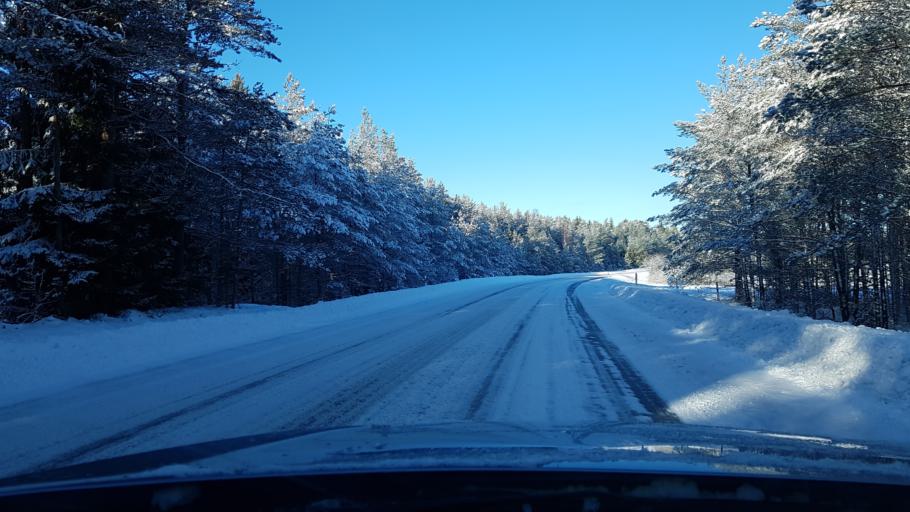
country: EE
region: Hiiumaa
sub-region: Kaerdla linn
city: Kardla
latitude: 58.9461
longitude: 22.7723
